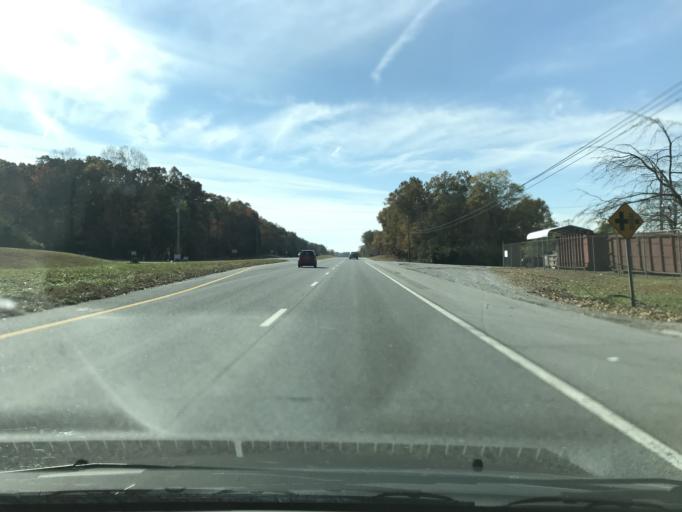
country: US
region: Tennessee
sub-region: Coffee County
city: Manchester
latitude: 35.4225
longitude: -86.1120
